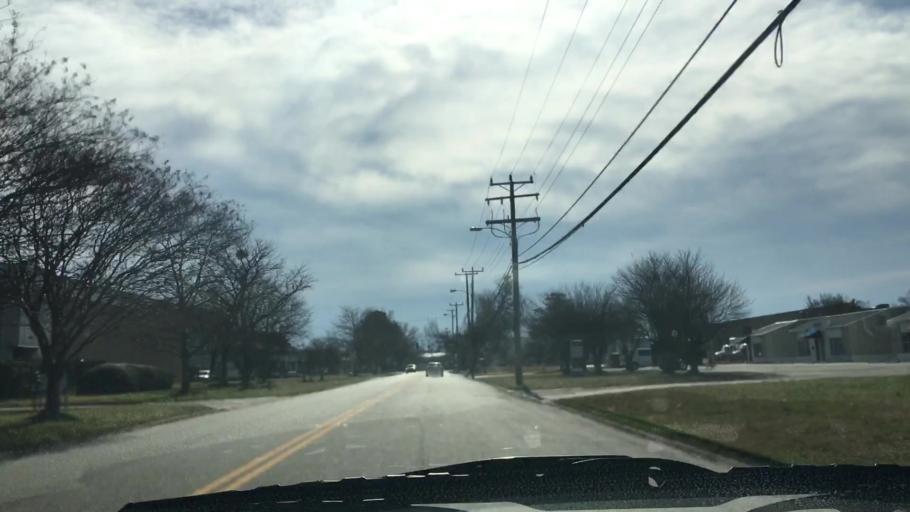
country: US
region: Virginia
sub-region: City of Norfolk
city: Norfolk
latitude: 36.8635
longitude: -76.2351
